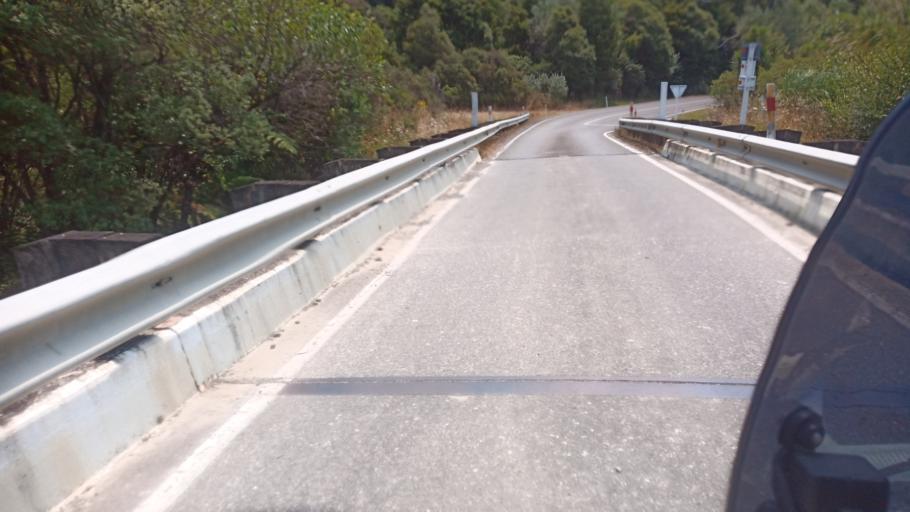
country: NZ
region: Bay of Plenty
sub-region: Opotiki District
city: Opotiki
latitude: -37.5926
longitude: 178.1526
